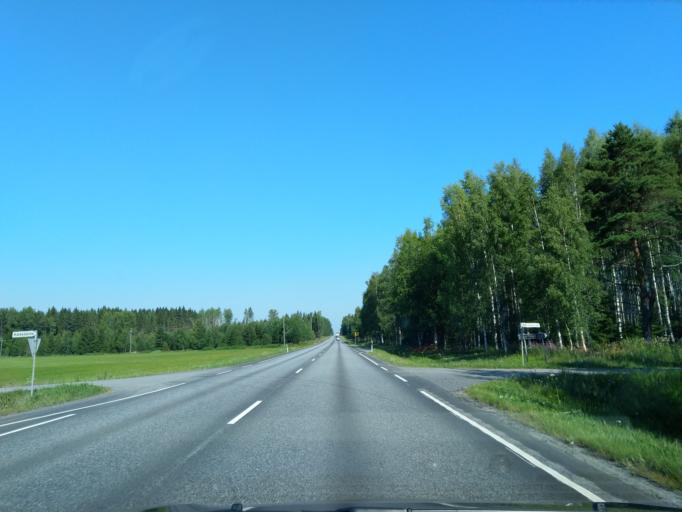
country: FI
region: Varsinais-Suomi
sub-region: Loimaa
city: Alastaro
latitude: 61.0690
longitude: 22.9246
